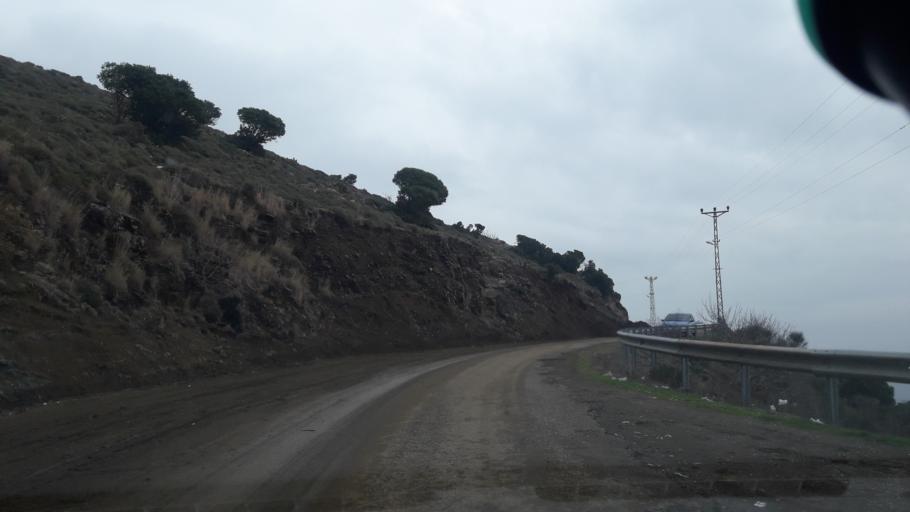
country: TR
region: Sinop
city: Sinop
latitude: 42.0176
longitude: 35.2011
